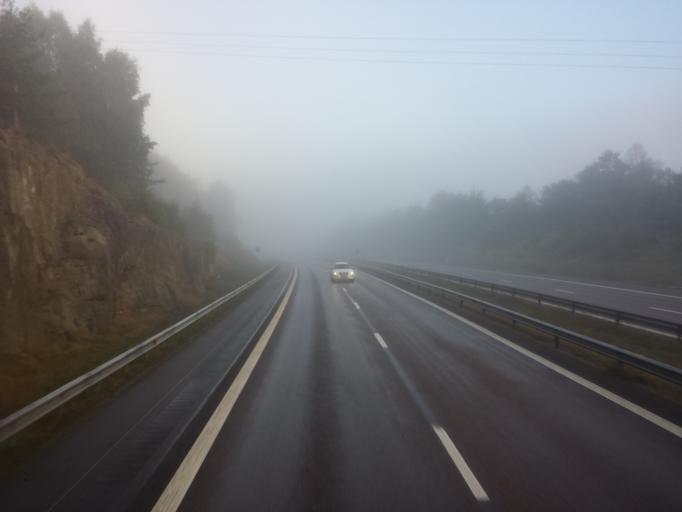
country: SE
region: Halland
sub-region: Kungsbacka Kommun
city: Fjaeras kyrkby
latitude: 57.4265
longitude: 12.1620
